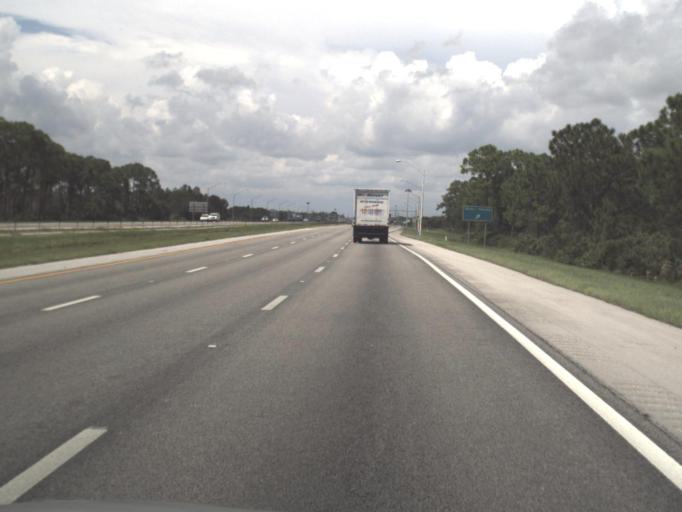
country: US
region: Florida
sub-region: Charlotte County
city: Charlotte Park
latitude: 26.8713
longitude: -81.9763
